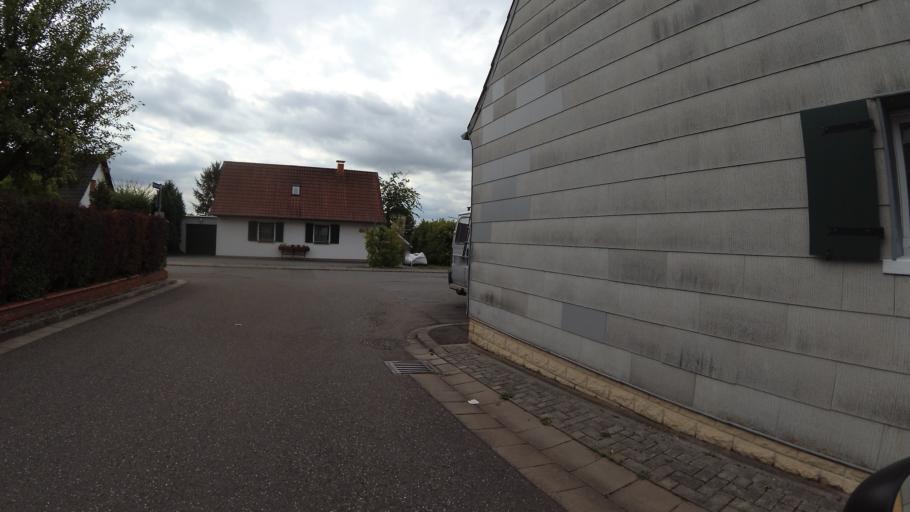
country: FR
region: Lorraine
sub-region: Departement de la Moselle
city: Sarreguemines
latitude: 49.1296
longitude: 7.0624
